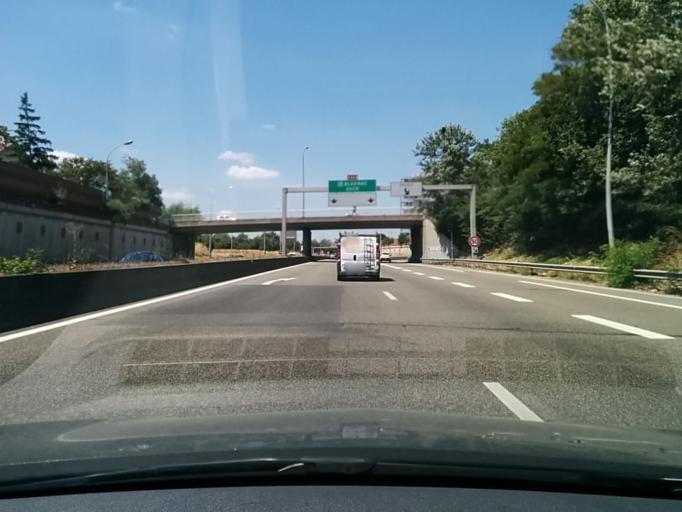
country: FR
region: Midi-Pyrenees
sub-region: Departement de la Haute-Garonne
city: Blagnac
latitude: 43.6052
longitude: 1.3966
